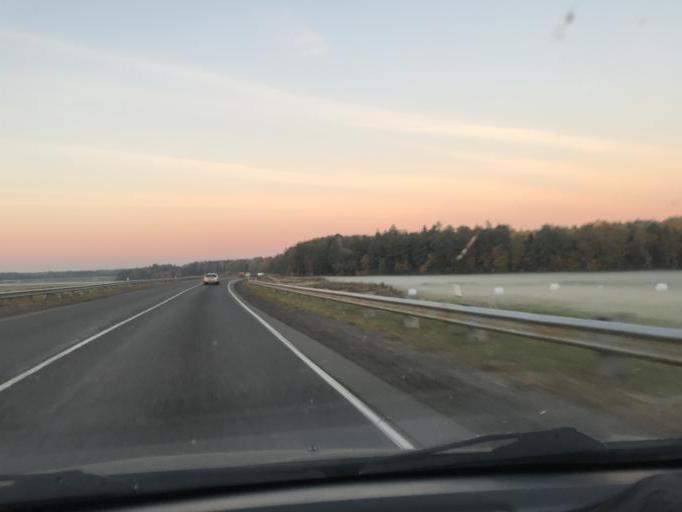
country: BY
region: Mogilev
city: Babruysk
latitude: 53.1966
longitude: 29.0570
